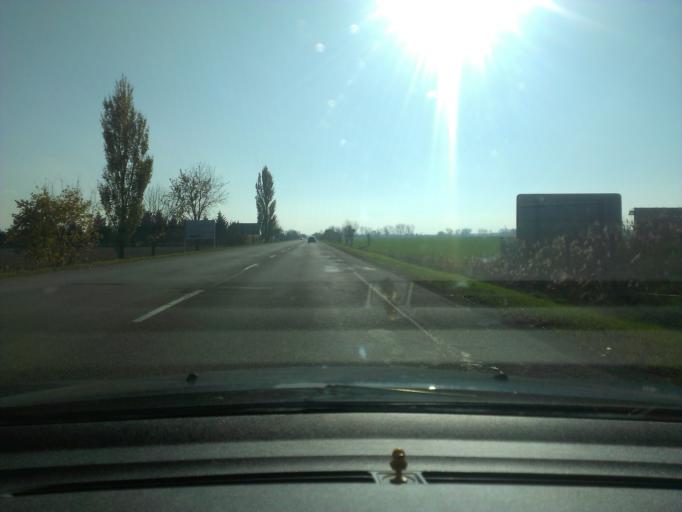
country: SK
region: Nitriansky
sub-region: Okres Nove Zamky
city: Nove Zamky
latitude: 47.9620
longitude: 18.1874
